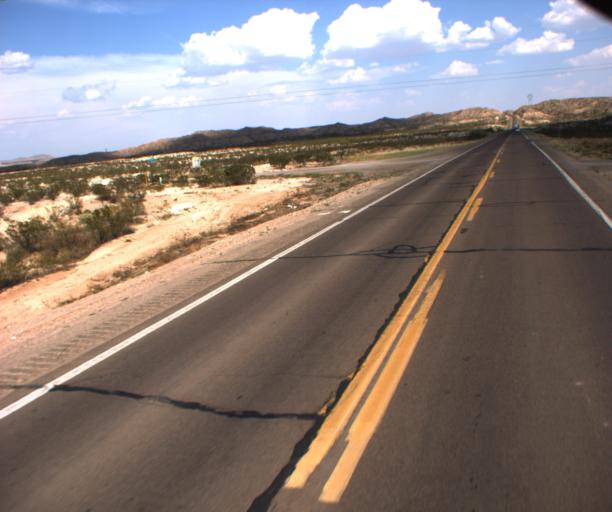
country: US
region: Arizona
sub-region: Greenlee County
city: Clifton
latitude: 32.7629
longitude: -109.1426
